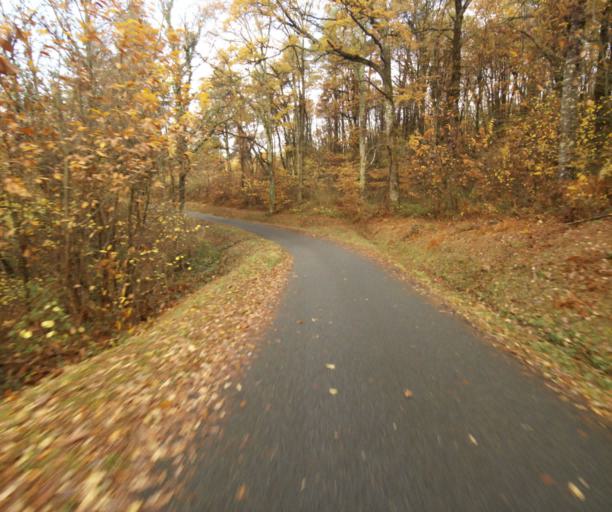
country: FR
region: Limousin
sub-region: Departement de la Correze
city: Cornil
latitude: 45.2230
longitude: 1.6574
